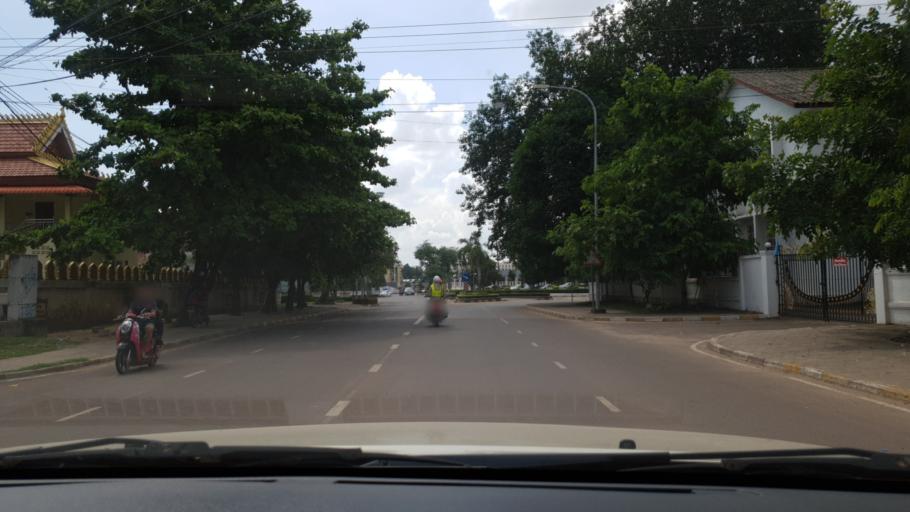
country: LA
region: Vientiane
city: Vientiane
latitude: 17.9692
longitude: 102.6188
